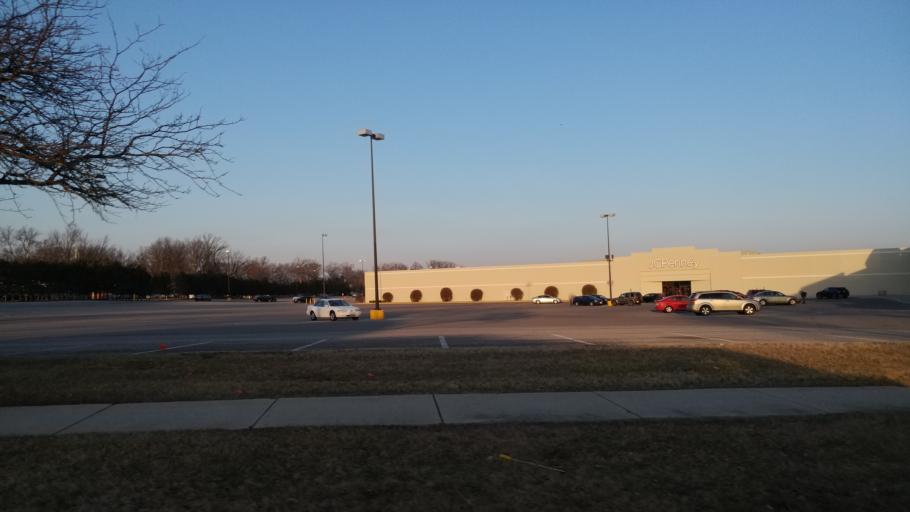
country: US
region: Ohio
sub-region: Hancock County
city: Findlay
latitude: 41.0547
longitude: -83.6164
